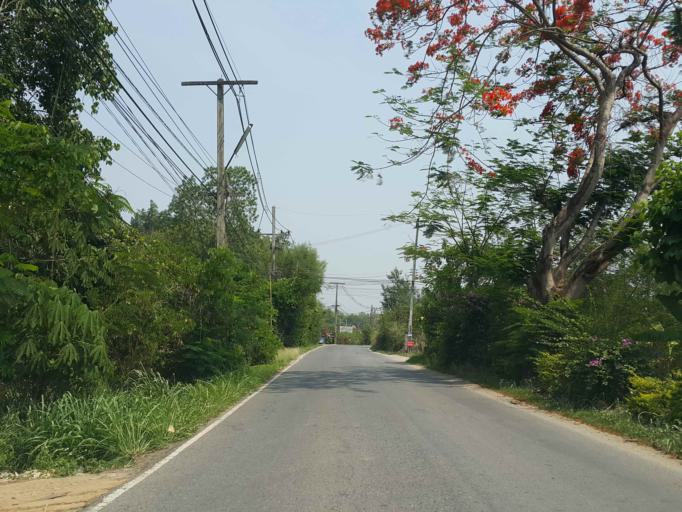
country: TH
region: Chiang Mai
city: San Sai
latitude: 18.8819
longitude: 98.9796
